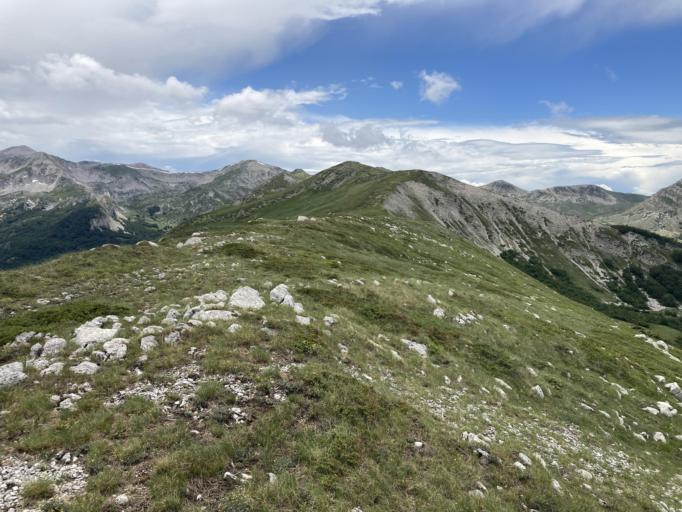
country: IT
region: Abruzzo
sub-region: Provincia dell' Aquila
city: Rocca di Cambio
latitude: 42.1969
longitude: 13.4362
